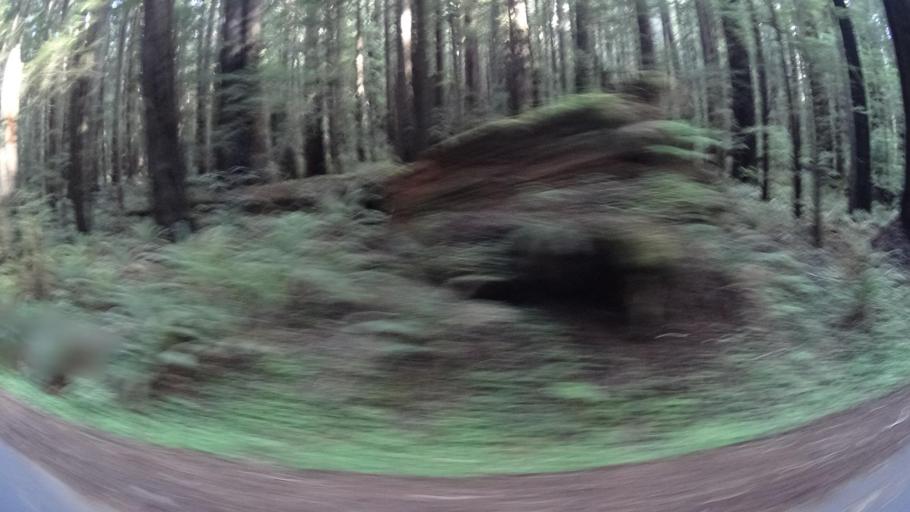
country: US
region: California
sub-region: Humboldt County
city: Rio Dell
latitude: 40.3513
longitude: -123.9975
